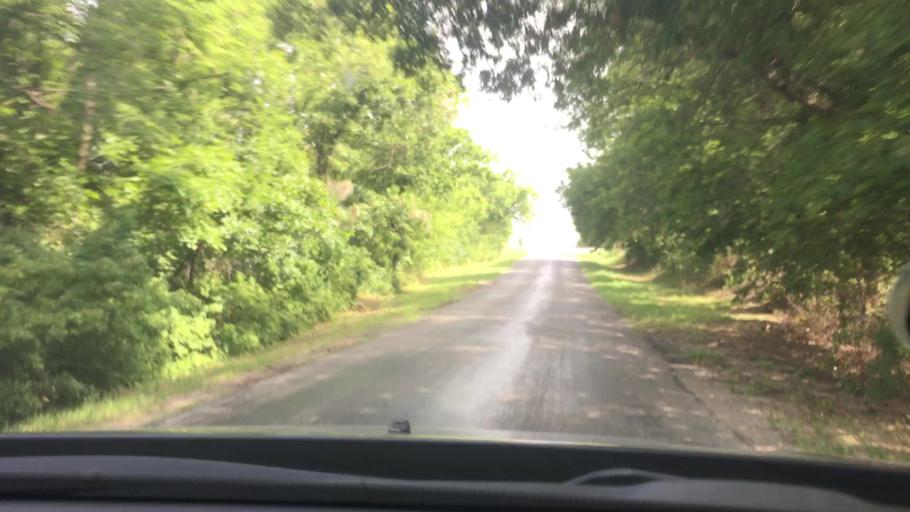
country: US
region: Oklahoma
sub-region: Garvin County
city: Pauls Valley
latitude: 34.8100
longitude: -97.1956
